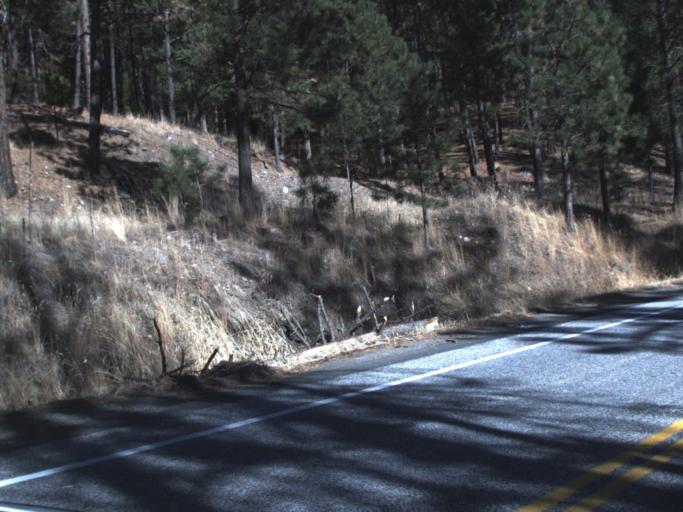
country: US
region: Washington
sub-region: Ferry County
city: Republic
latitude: 48.6494
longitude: -118.7169
